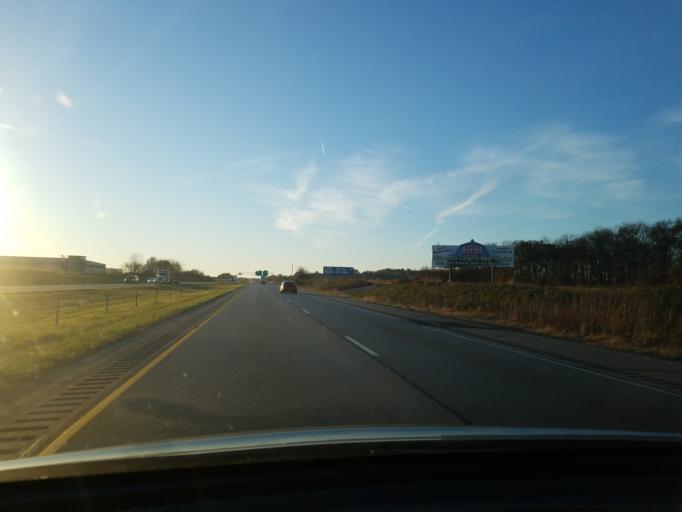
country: US
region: Indiana
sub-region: Gibson County
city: Haubstadt
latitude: 38.1698
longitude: -87.4577
